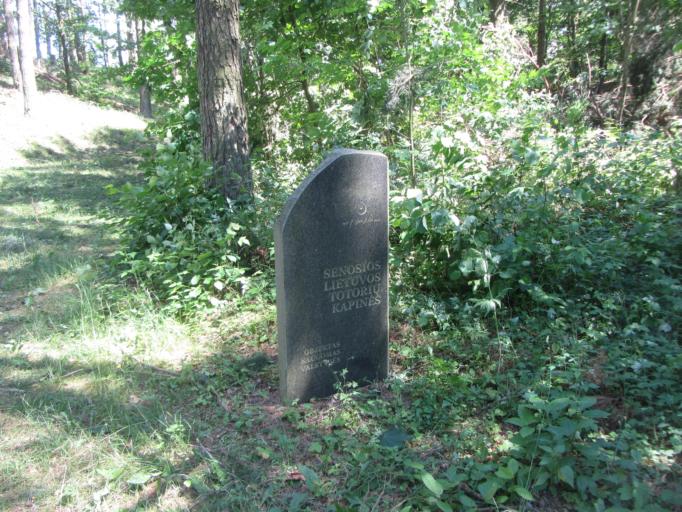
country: LT
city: Jieznas
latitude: 54.4744
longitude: 24.1763
